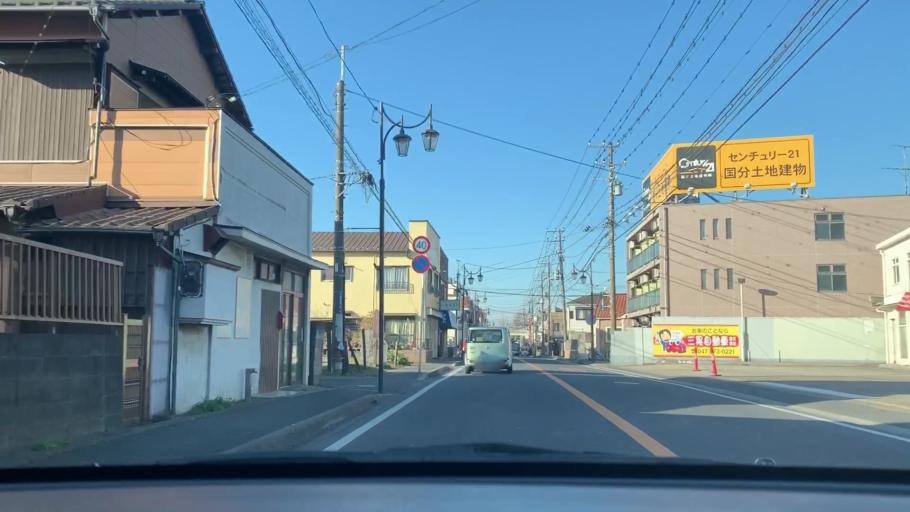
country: JP
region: Chiba
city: Matsudo
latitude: 35.7501
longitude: 139.9031
